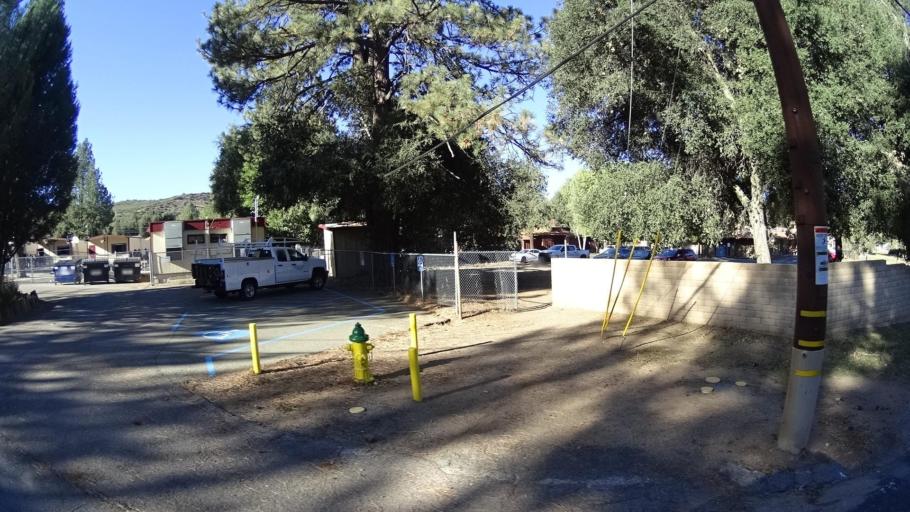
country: US
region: California
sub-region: San Diego County
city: Pine Valley
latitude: 32.8207
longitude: -116.5260
